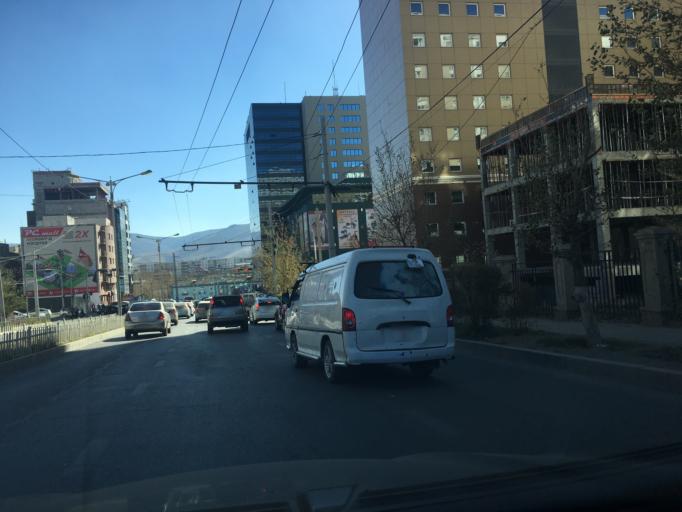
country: MN
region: Ulaanbaatar
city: Ulaanbaatar
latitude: 47.9159
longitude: 106.8910
